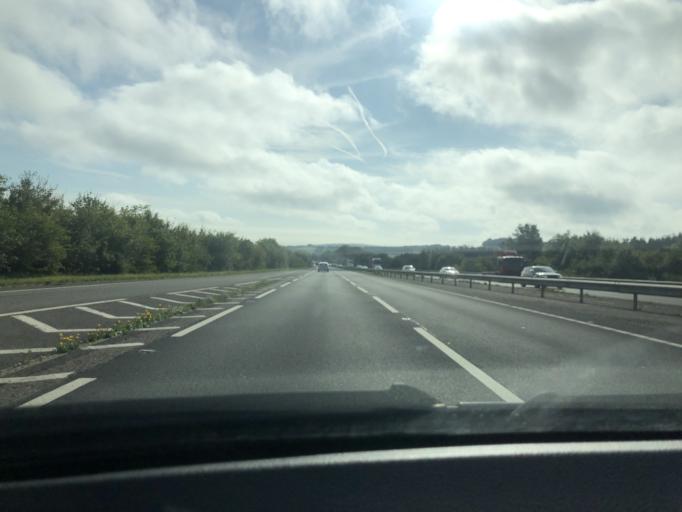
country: GB
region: England
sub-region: Devon
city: Crediton
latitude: 50.7268
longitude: -3.7219
